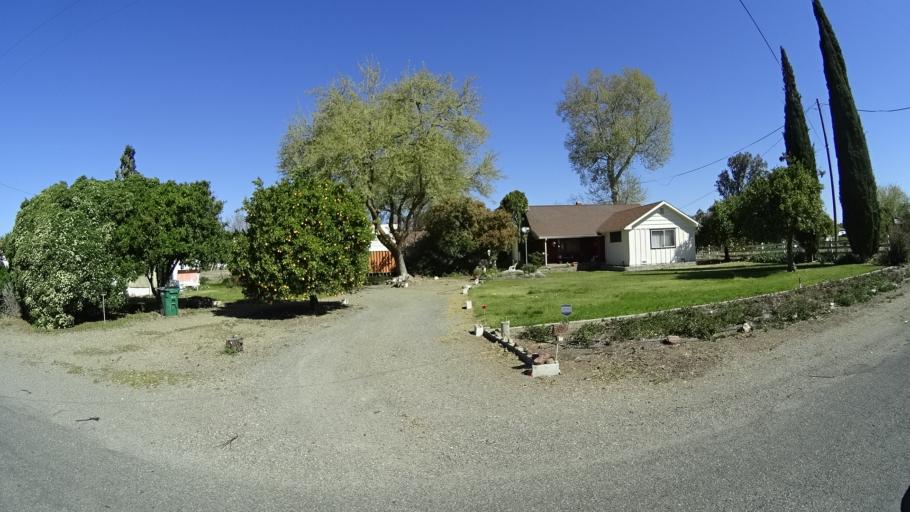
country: US
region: California
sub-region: Glenn County
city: Orland
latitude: 39.7113
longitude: -122.2099
